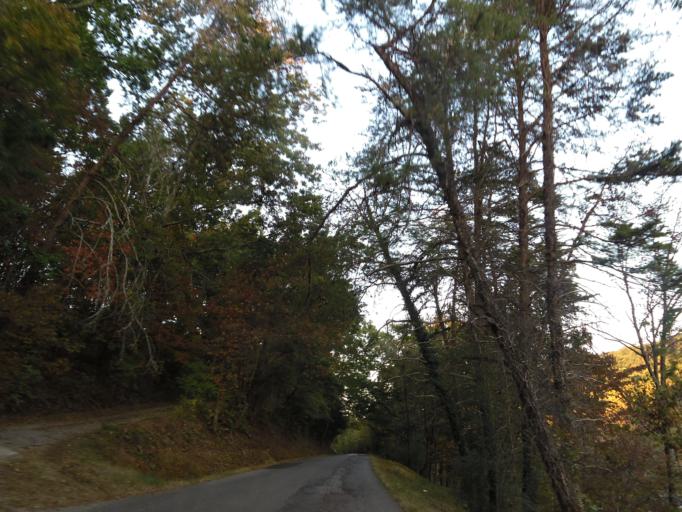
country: US
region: Tennessee
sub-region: Blount County
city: Eagleton Village
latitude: 35.8359
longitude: -83.9259
